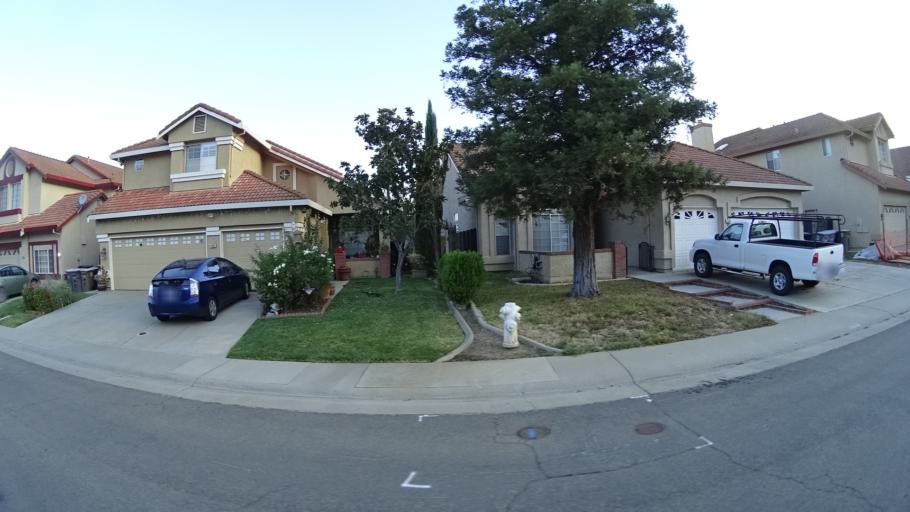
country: US
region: California
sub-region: Sacramento County
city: Laguna
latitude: 38.4328
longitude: -121.4522
